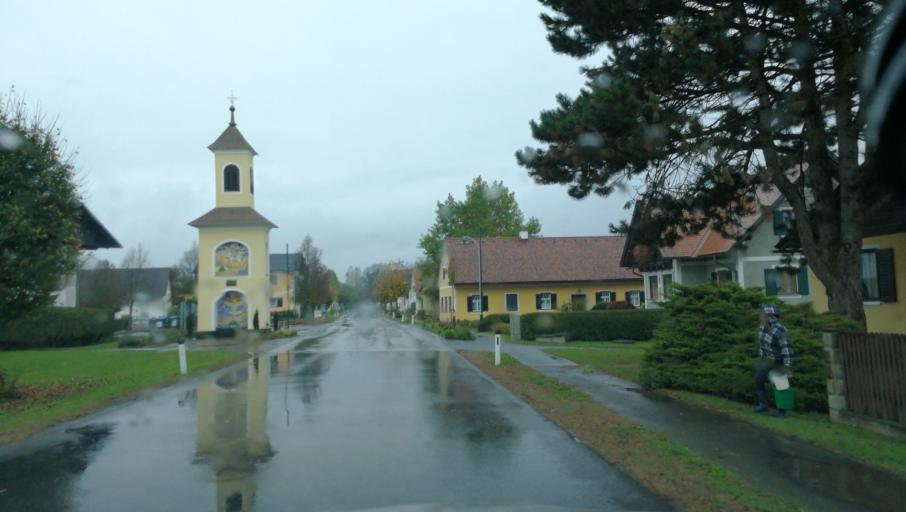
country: AT
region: Styria
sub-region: Politischer Bezirk Suedoststeiermark
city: Weinburg am Sassbach
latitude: 46.7342
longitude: 15.7099
